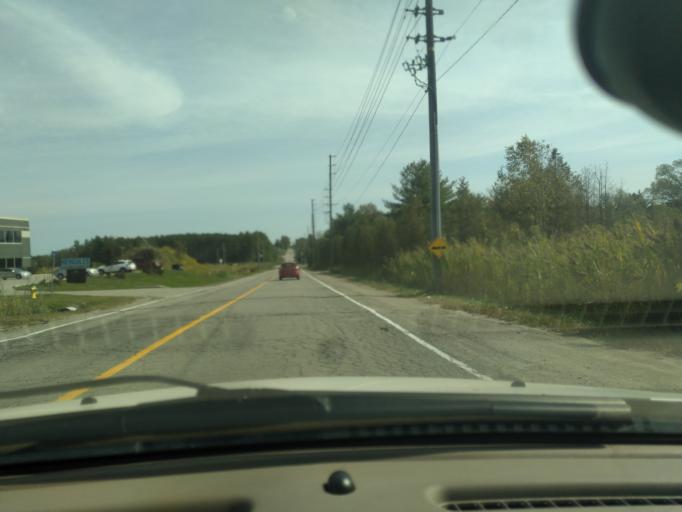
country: CA
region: Ontario
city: Innisfil
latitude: 44.3278
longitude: -79.6629
